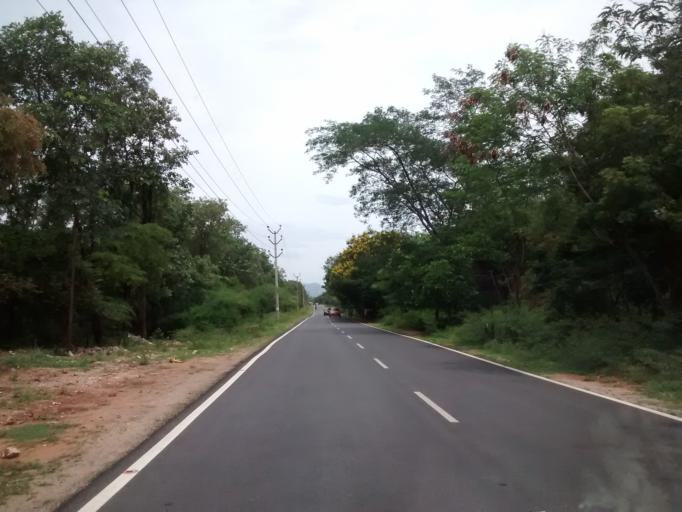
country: IN
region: Andhra Pradesh
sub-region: Chittoor
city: Tirupati
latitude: 13.6308
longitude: 79.3837
